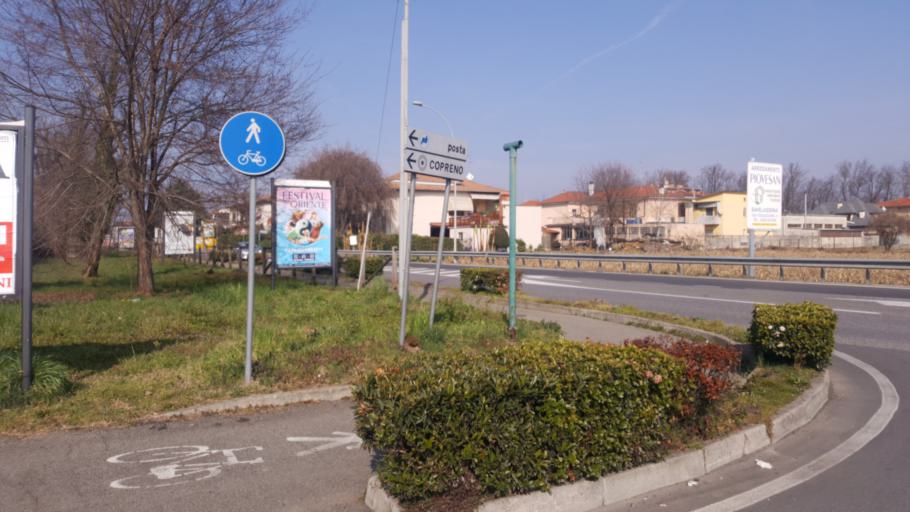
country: IT
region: Lombardy
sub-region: Provincia di Monza e Brianza
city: Lentate sul Seveso
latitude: 45.6859
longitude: 9.1104
